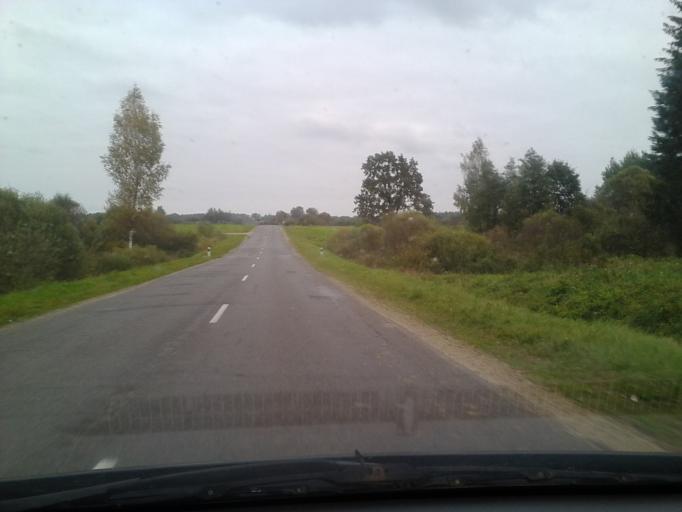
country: BY
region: Vitebsk
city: Pastavy
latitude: 55.1187
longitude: 26.9240
